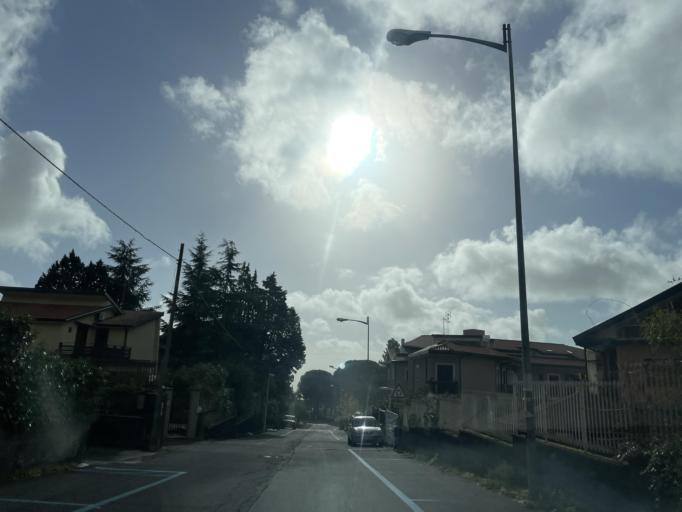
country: IT
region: Sicily
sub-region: Catania
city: Nicolosi
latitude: 37.6193
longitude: 15.0248
